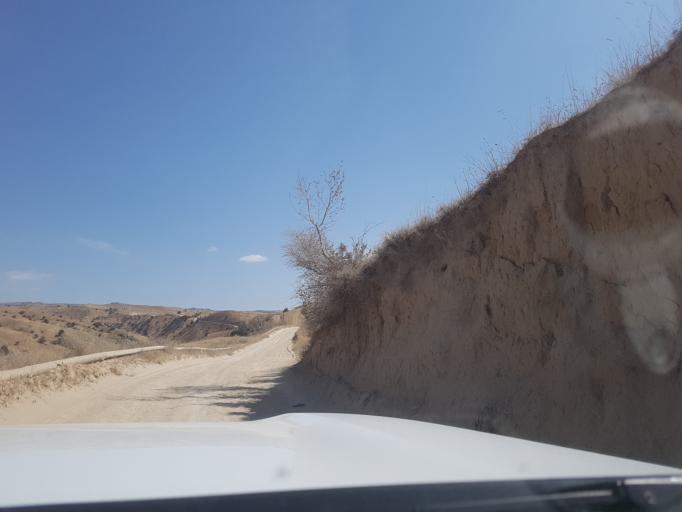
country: TM
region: Ahal
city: Baharly
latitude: 38.2752
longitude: 56.9033
